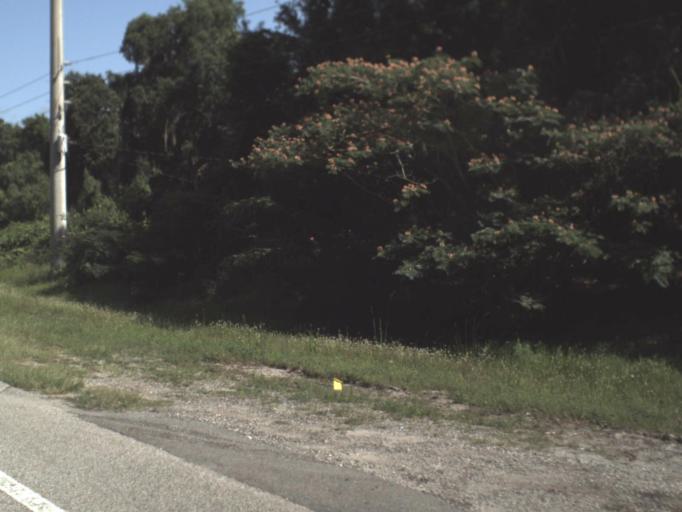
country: US
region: Florida
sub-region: Saint Johns County
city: Saint Augustine
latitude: 29.9466
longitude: -81.4458
